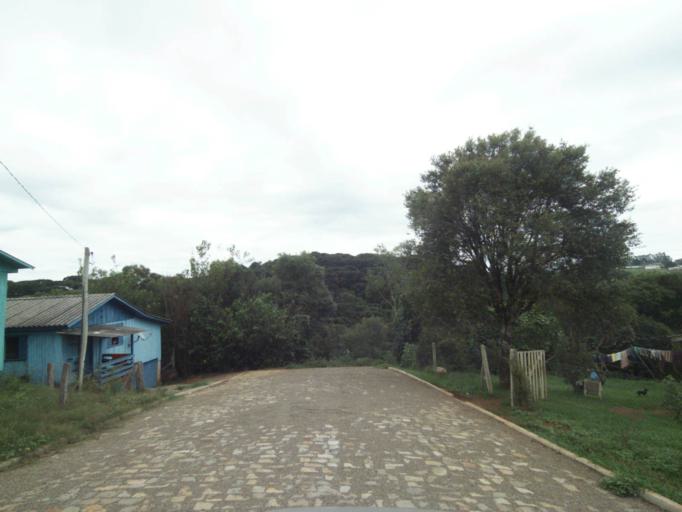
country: BR
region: Rio Grande do Sul
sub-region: Lagoa Vermelha
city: Lagoa Vermelha
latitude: -28.2175
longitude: -51.5404
